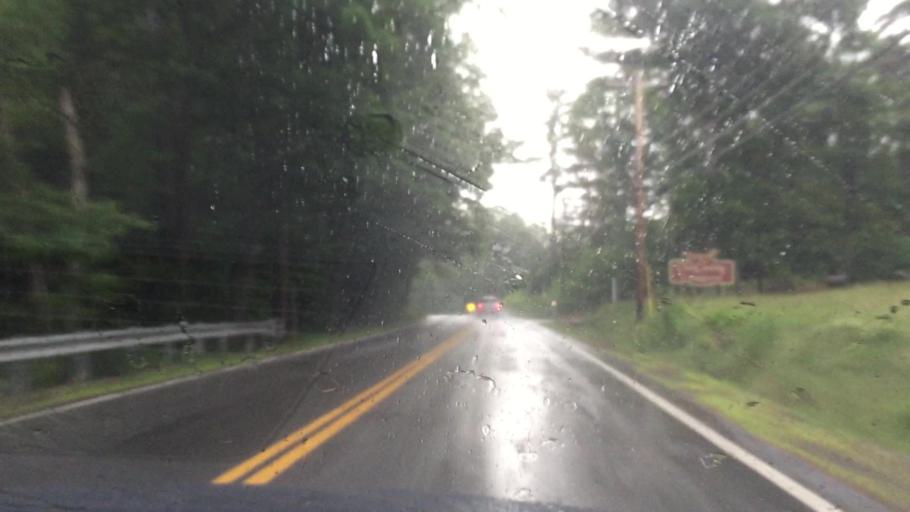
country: US
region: New Hampshire
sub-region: Grafton County
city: Holderness
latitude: 43.7192
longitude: -71.5386
